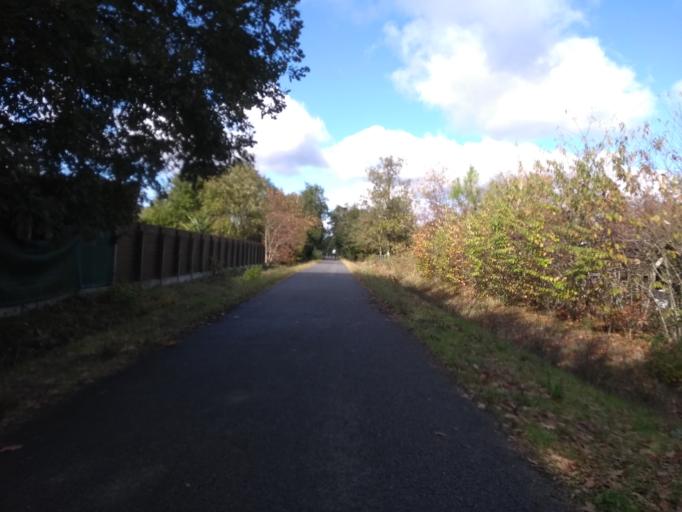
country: FR
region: Aquitaine
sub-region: Departement de la Gironde
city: Saint-Aubin-de-Medoc
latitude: 44.7877
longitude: -0.7000
